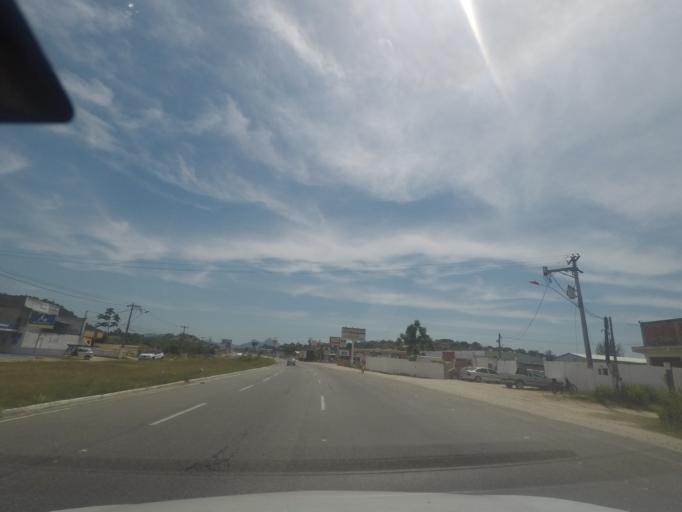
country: BR
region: Rio de Janeiro
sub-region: Marica
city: Marica
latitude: -22.9305
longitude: -42.8733
